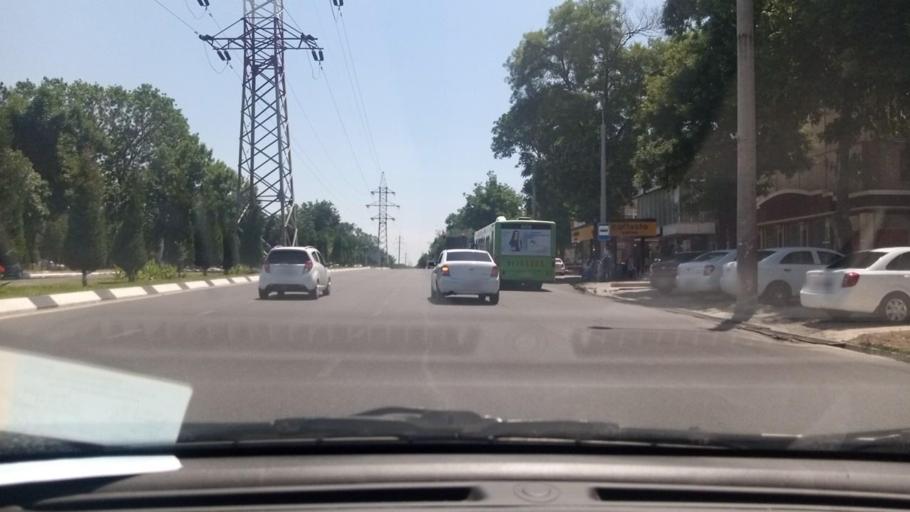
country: UZ
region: Toshkent Shahri
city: Tashkent
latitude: 41.2935
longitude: 69.1940
